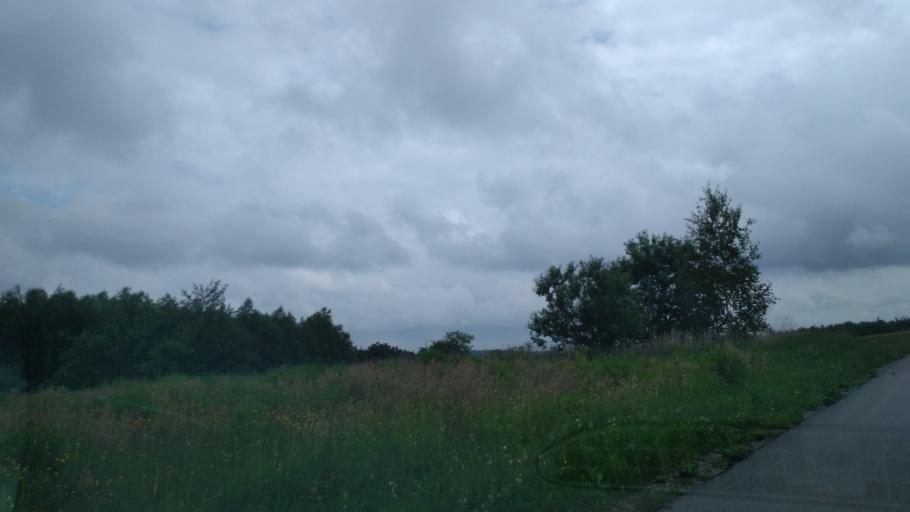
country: PL
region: Subcarpathian Voivodeship
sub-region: Powiat przemyski
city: Nienadowa
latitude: 49.8654
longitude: 22.4071
